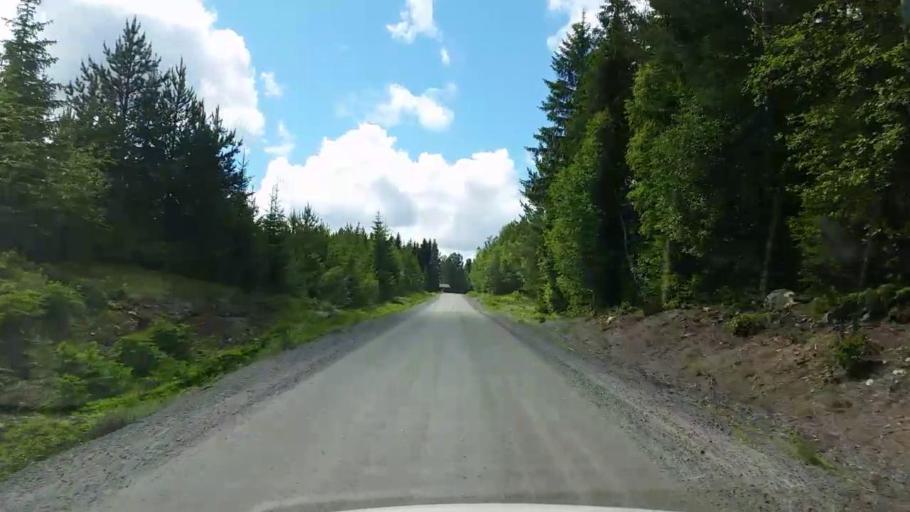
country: SE
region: Gaevleborg
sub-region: Bollnas Kommun
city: Vittsjo
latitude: 61.0897
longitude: 16.1989
